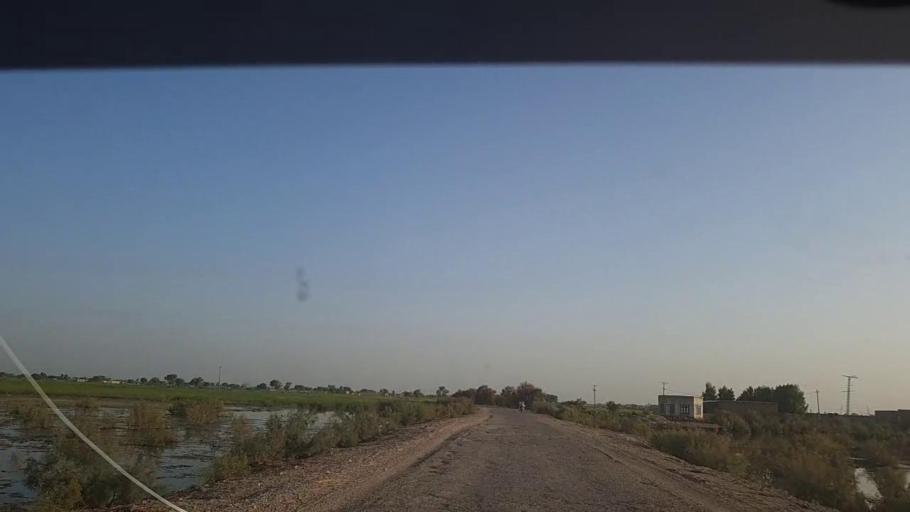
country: PK
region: Sindh
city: Thul
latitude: 28.1393
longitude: 68.8871
